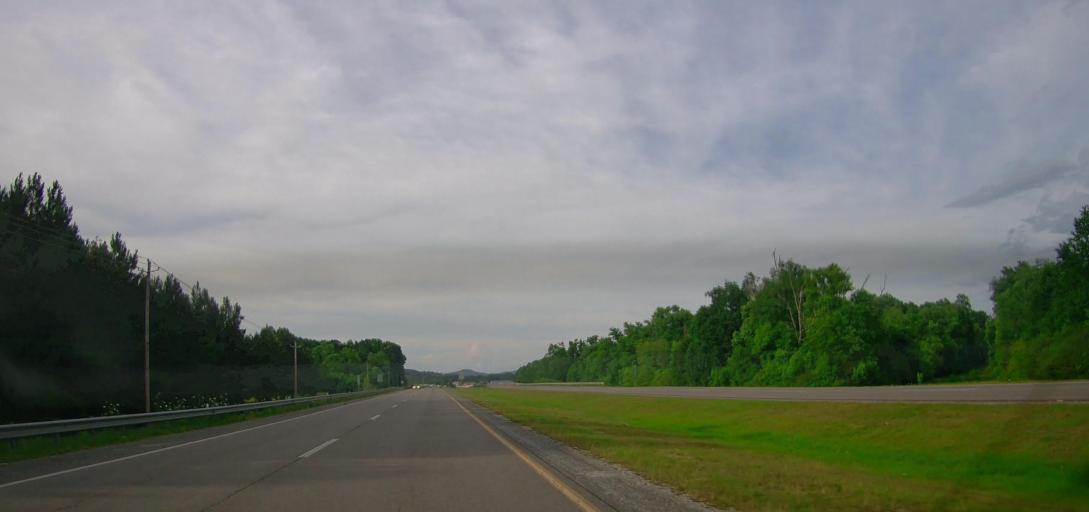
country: US
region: Alabama
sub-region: Calhoun County
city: Oxford
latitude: 33.5824
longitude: -85.8485
